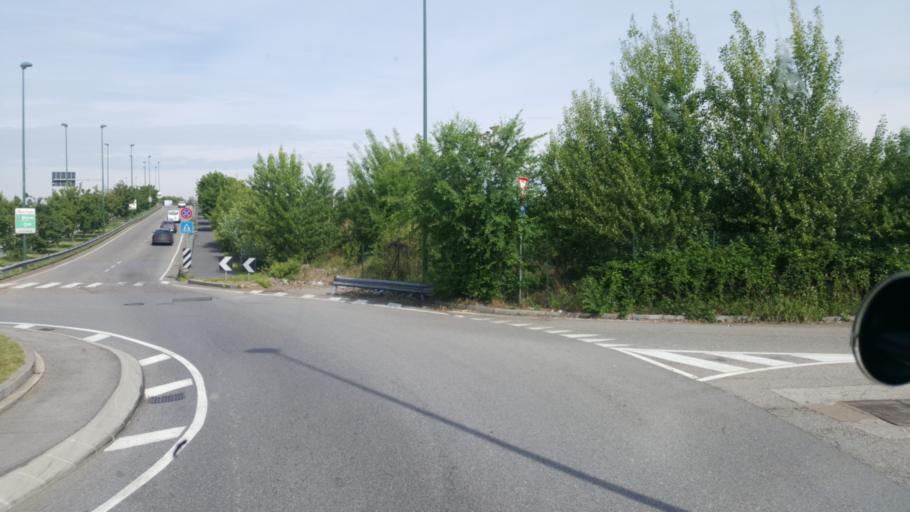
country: IT
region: Lombardy
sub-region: Citta metropolitana di Milano
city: Sesto San Giovanni
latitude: 45.5504
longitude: 9.2531
